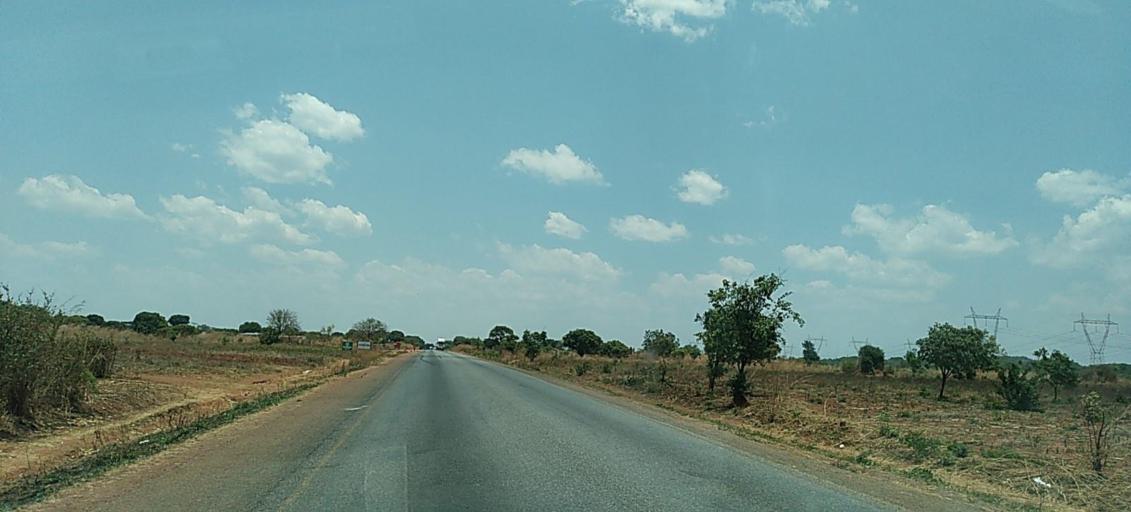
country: ZM
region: Central
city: Kapiri Mposhi
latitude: -13.7051
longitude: 28.6300
